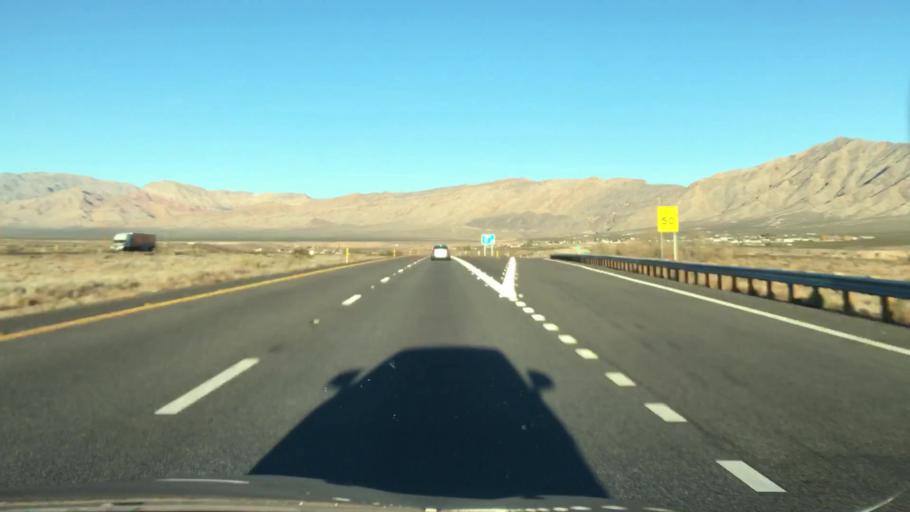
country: US
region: Arizona
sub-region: Mohave County
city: Beaver Dam
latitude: 36.8865
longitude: -113.9367
